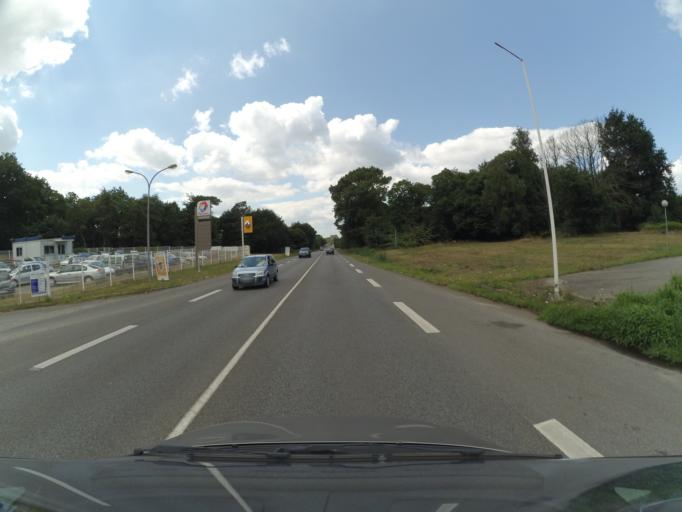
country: FR
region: Brittany
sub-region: Departement du Morbihan
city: Lanester
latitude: 47.7619
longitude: -3.2928
